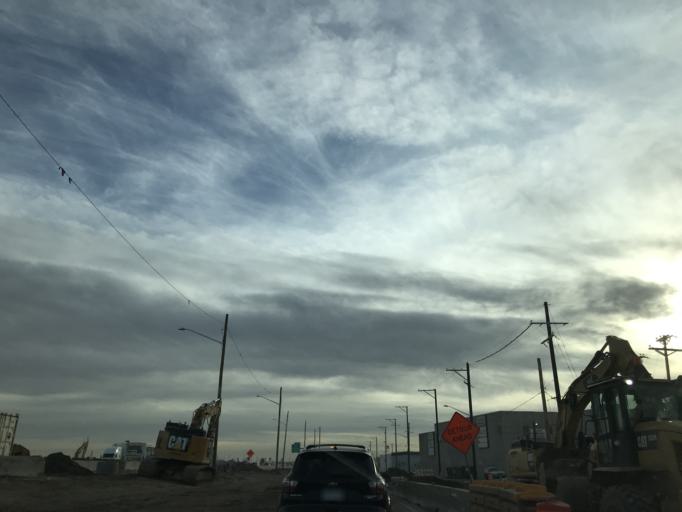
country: US
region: Colorado
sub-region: Adams County
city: Commerce City
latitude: 39.7791
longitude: -104.9276
